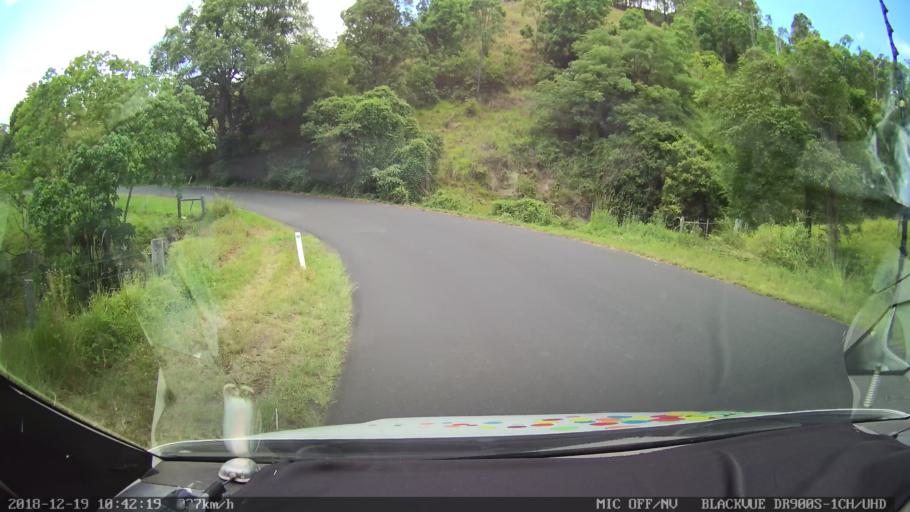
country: AU
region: New South Wales
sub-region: Lismore Municipality
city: Nimbin
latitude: -28.5921
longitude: 153.1666
